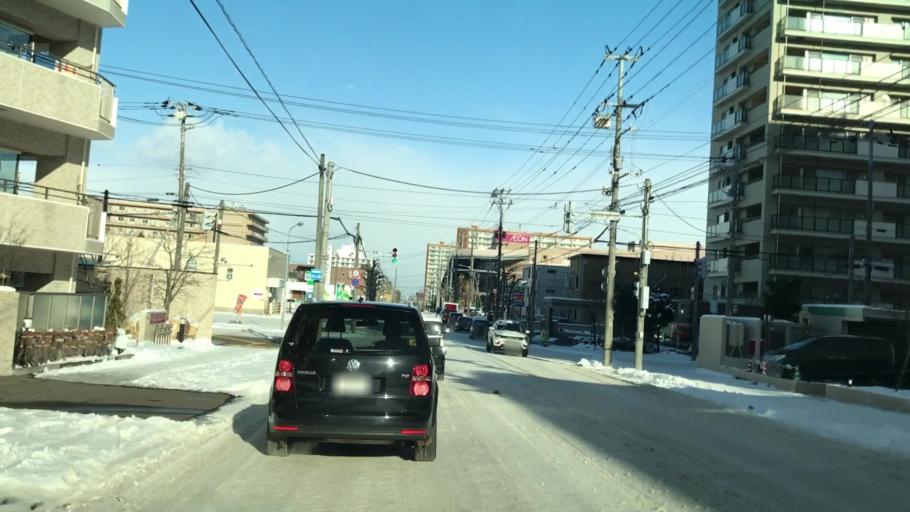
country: JP
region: Hokkaido
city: Sapporo
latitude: 43.0949
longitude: 141.2734
